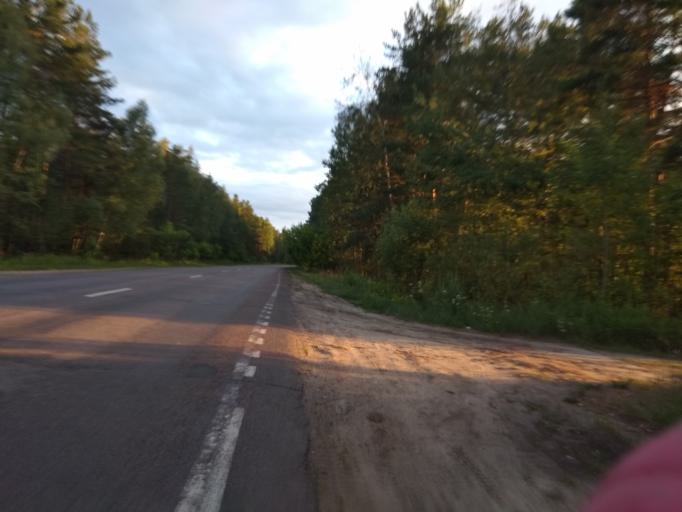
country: RU
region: Moskovskaya
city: Kerva
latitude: 55.5831
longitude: 39.6953
